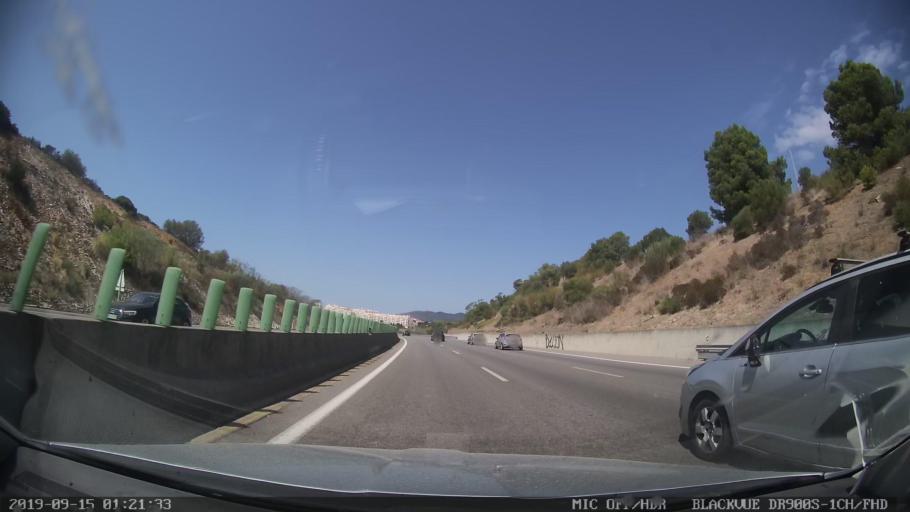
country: PT
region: Lisbon
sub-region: Cascais
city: Alcabideche
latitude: 38.7242
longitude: -9.4004
